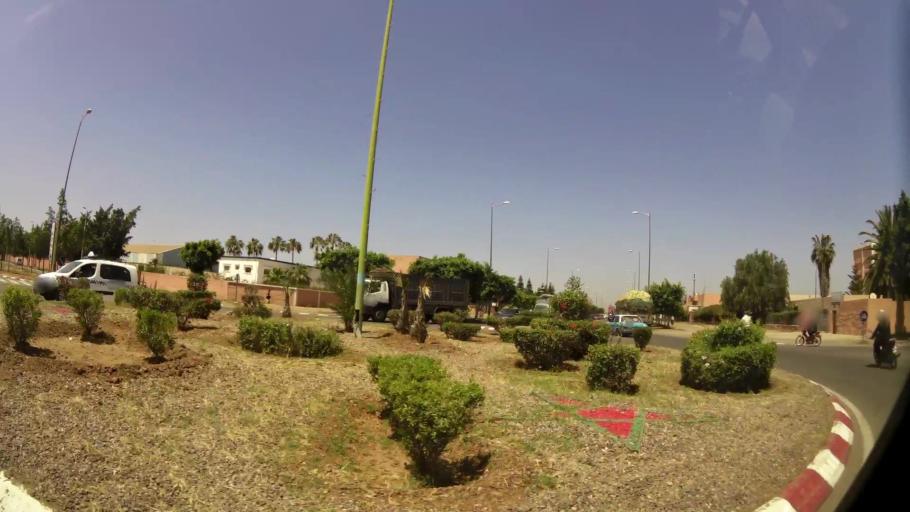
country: MA
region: Souss-Massa-Draa
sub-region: Inezgane-Ait Mellou
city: Inezgane
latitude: 30.3329
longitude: -9.4902
